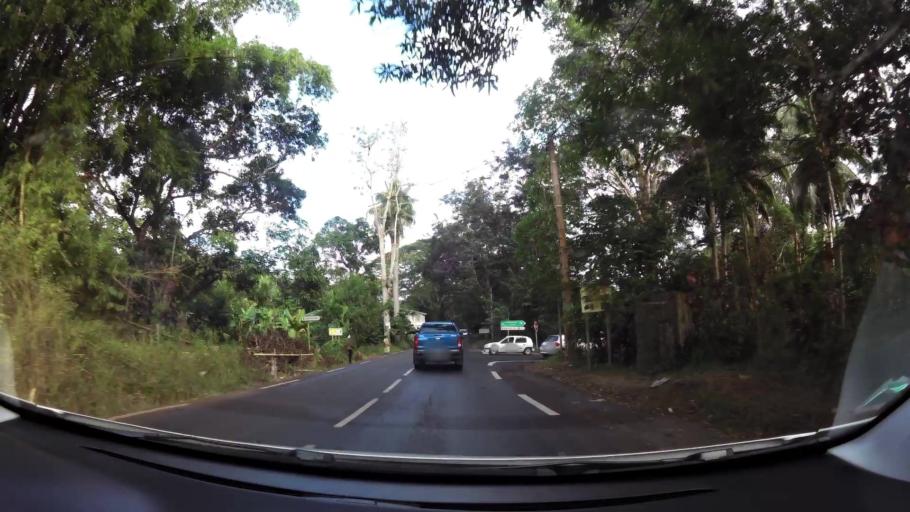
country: YT
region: Ouangani
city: Ouangani
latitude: -12.8342
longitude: 45.1390
